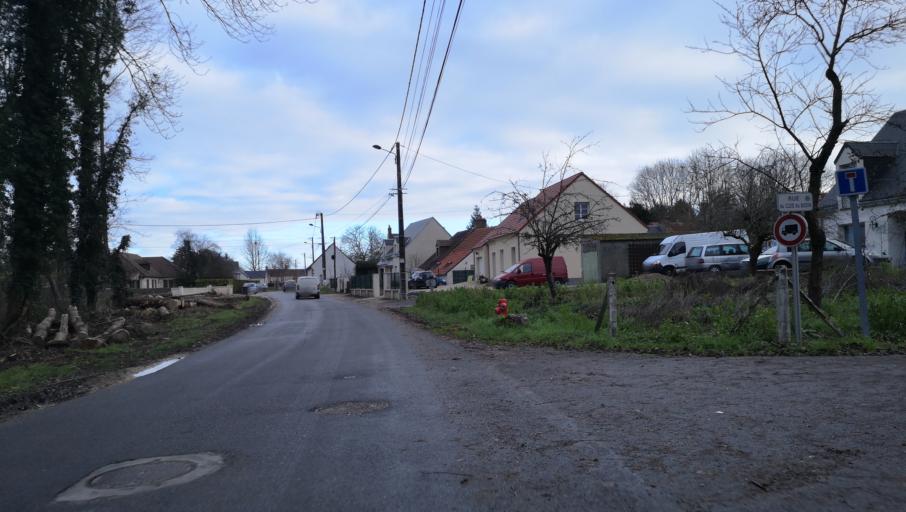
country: FR
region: Centre
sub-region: Departement du Loiret
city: Saint-Jean-de-Braye
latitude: 47.9097
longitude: 2.0005
